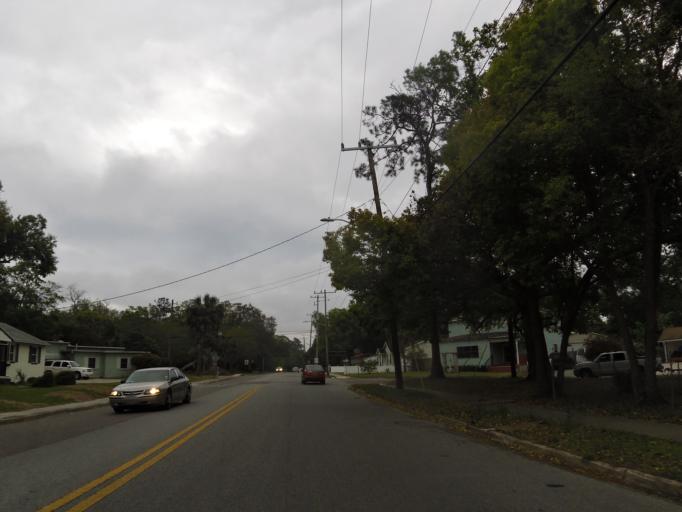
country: US
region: Florida
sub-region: Duval County
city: Jacksonville
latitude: 30.2966
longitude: -81.6305
